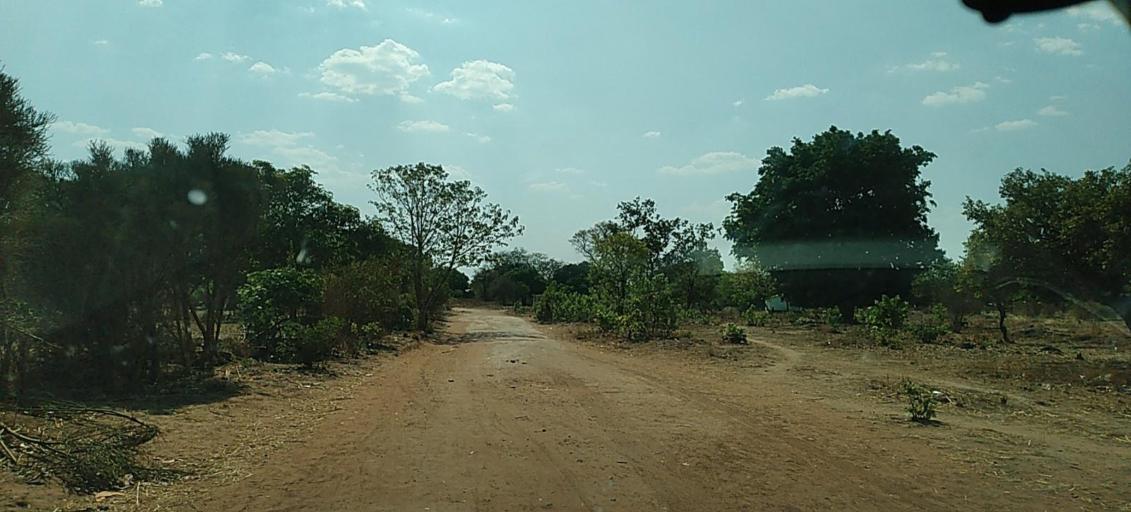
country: ZM
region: North-Western
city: Kalengwa
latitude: -13.1319
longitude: 25.0149
